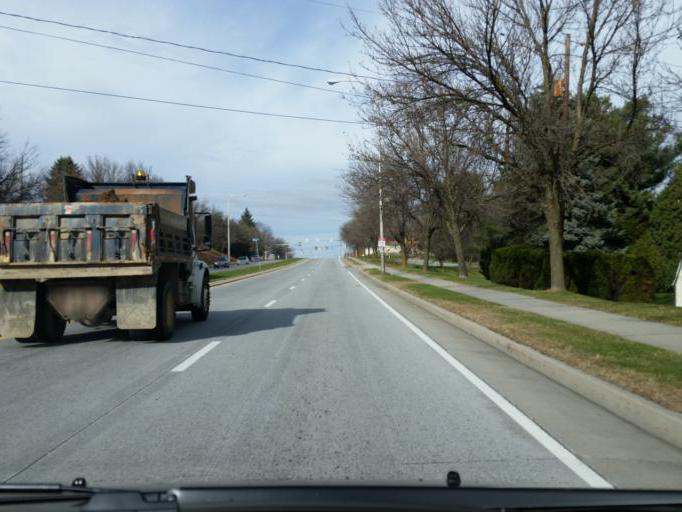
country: US
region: Pennsylvania
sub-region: Blair County
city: Altoona
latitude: 40.5028
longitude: -78.3945
